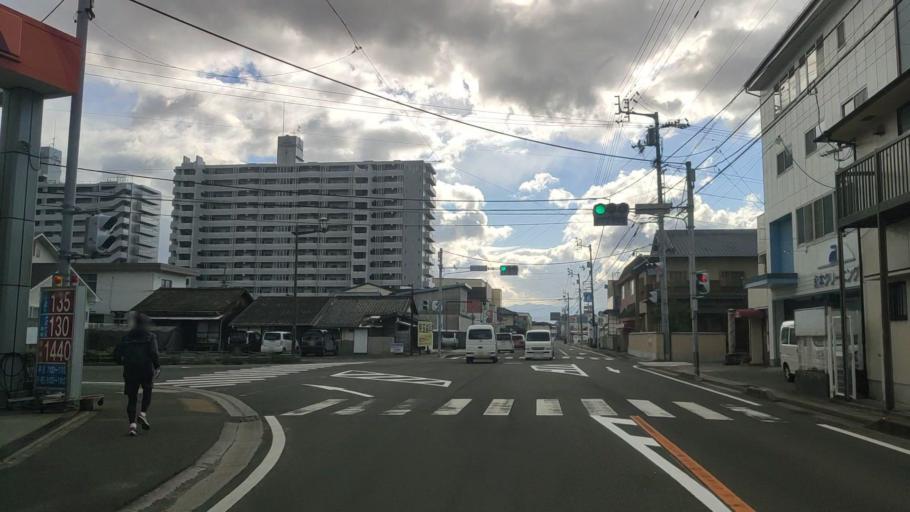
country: JP
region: Ehime
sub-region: Shikoku-chuo Shi
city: Matsuyama
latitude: 33.8679
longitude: 132.7180
